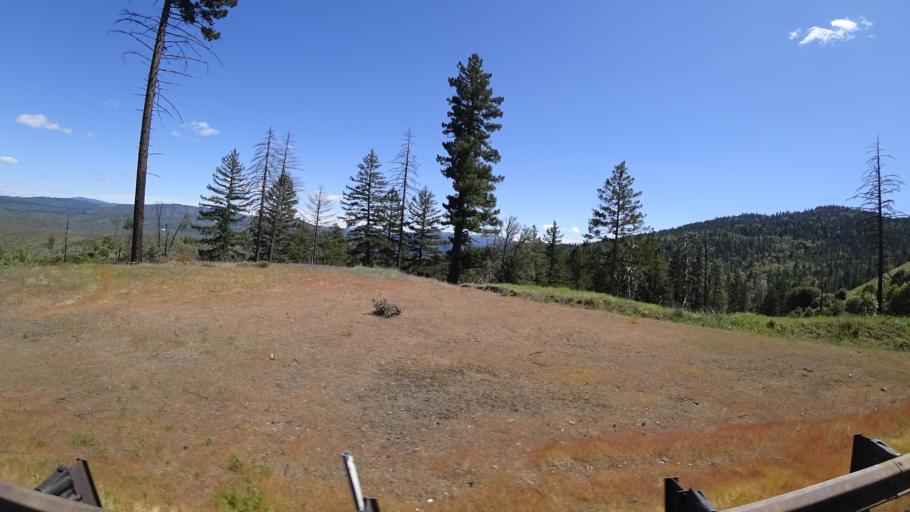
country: US
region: California
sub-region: Trinity County
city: Weaverville
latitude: 40.7409
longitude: -122.9798
